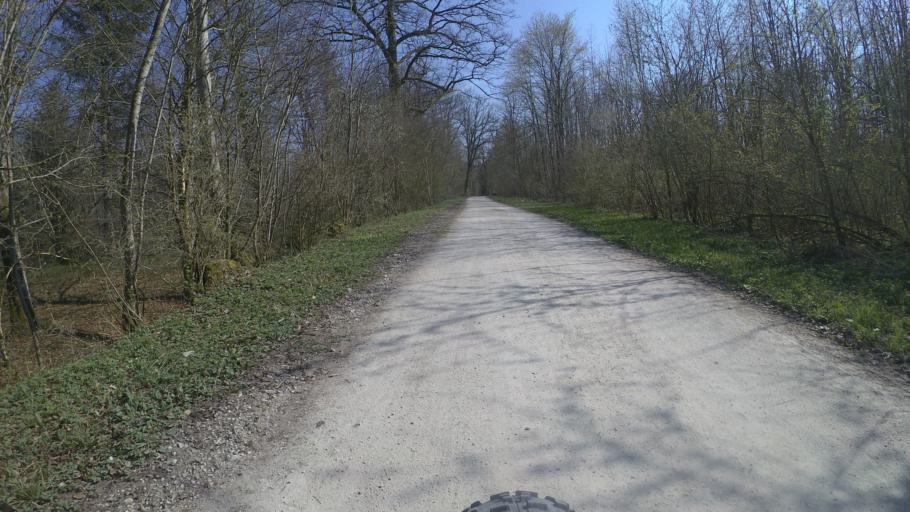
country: DE
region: Bavaria
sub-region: Upper Bavaria
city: Traunreut
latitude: 47.9492
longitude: 12.5850
